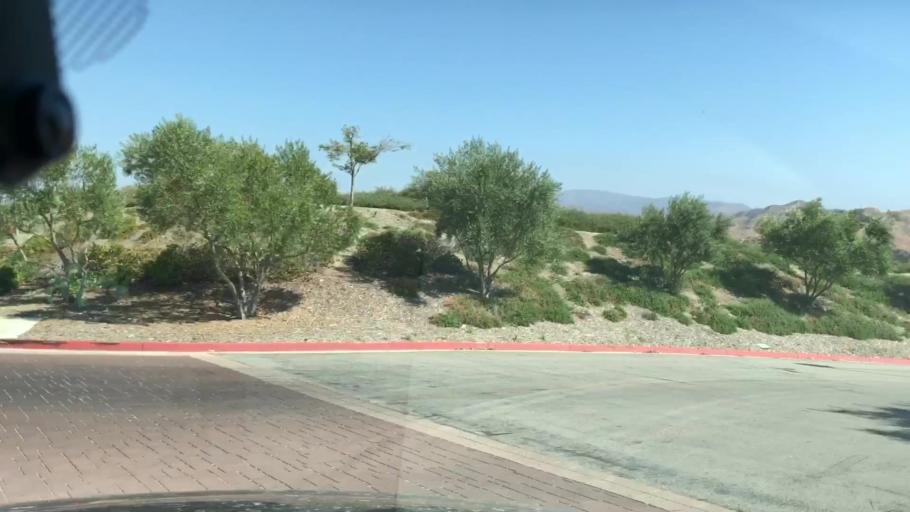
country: US
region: California
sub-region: Los Angeles County
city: Santa Clarita
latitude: 34.3949
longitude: -118.4601
